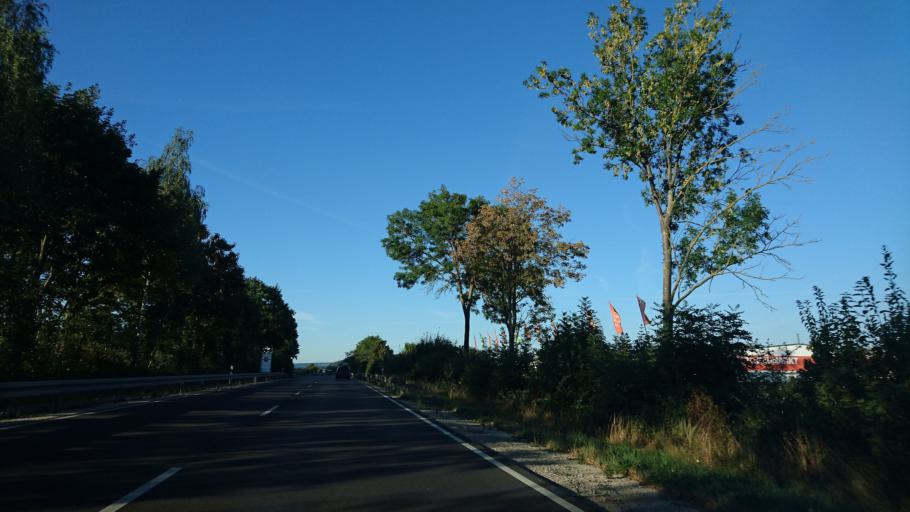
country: DE
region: Bavaria
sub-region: Regierungsbezirk Mittelfranken
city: Weissenburg in Bayern
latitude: 49.0085
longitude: 10.9561
